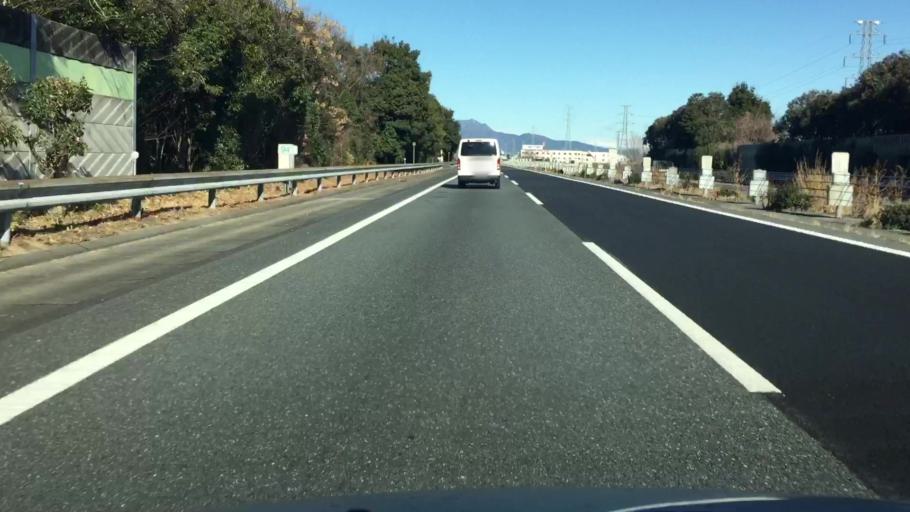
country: JP
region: Gunma
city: Kanekomachi
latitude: 36.3982
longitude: 139.0248
